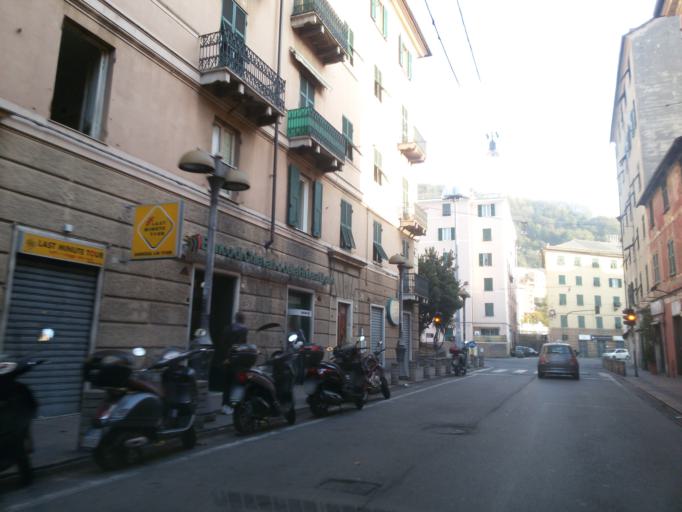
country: IT
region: Liguria
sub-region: Provincia di Genova
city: Genoa
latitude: 44.4292
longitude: 8.8928
